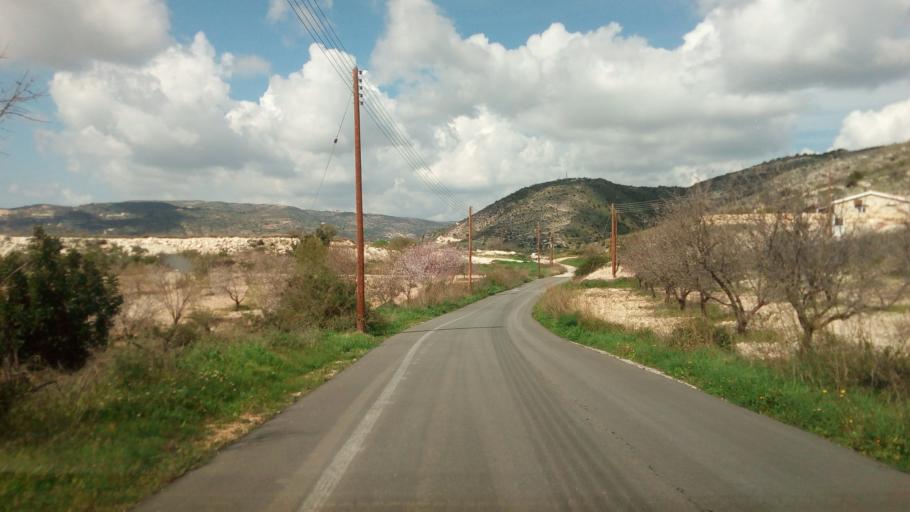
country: CY
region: Pafos
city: Mesogi
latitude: 34.7851
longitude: 32.5463
